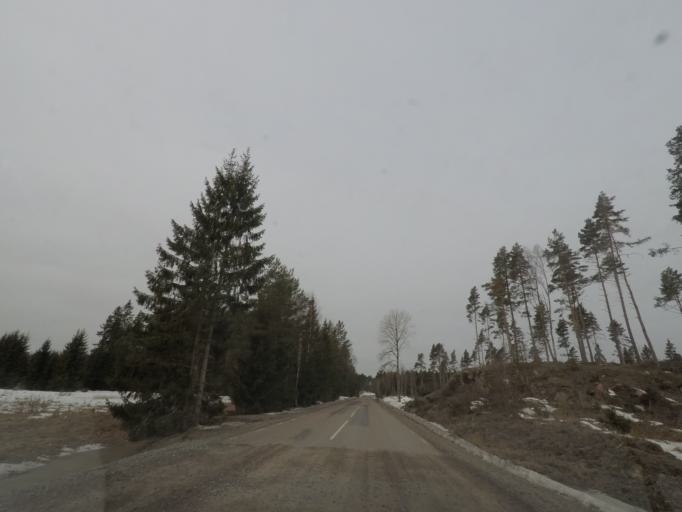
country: SE
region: Vaestmanland
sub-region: Vasteras
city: Skultuna
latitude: 59.7402
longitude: 16.3916
